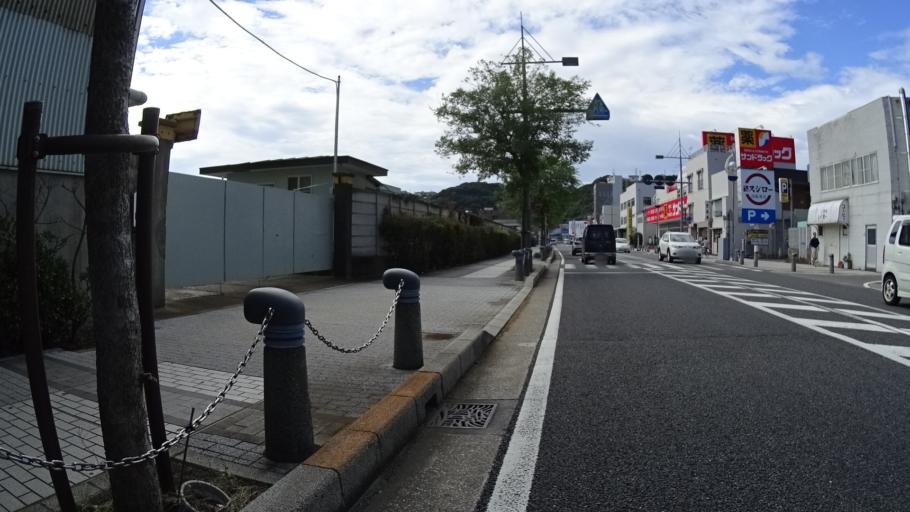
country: JP
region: Kanagawa
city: Yokosuka
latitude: 35.2486
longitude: 139.7150
